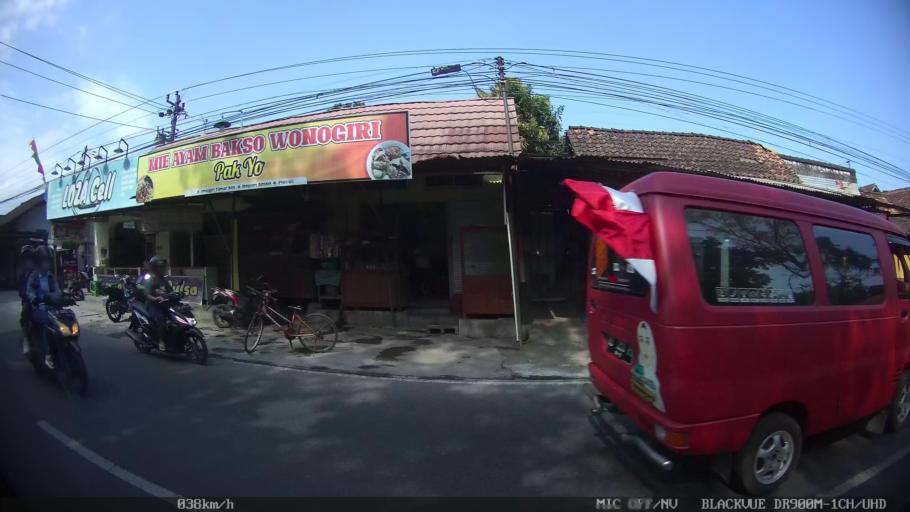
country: ID
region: Daerah Istimewa Yogyakarta
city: Sewon
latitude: -7.8632
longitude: 110.3893
